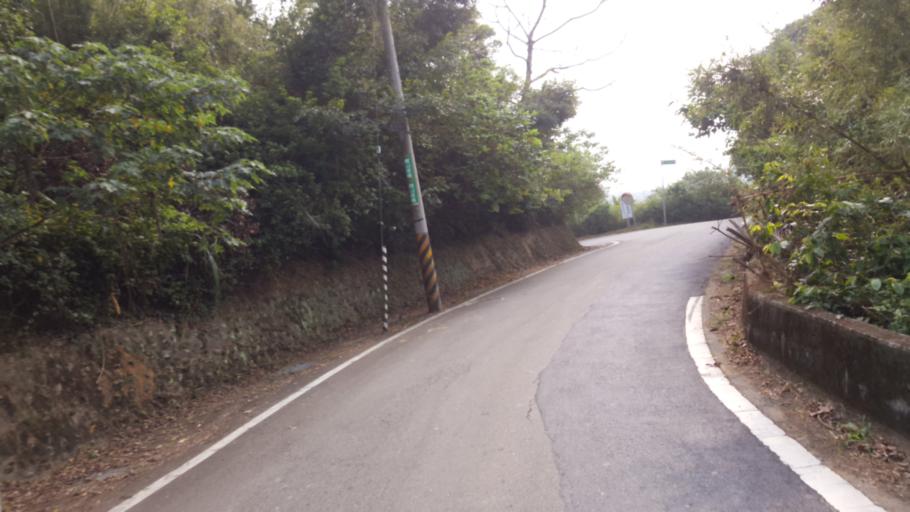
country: TW
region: Taiwan
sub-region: Hsinchu
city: Hsinchu
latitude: 24.7481
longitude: 120.9550
